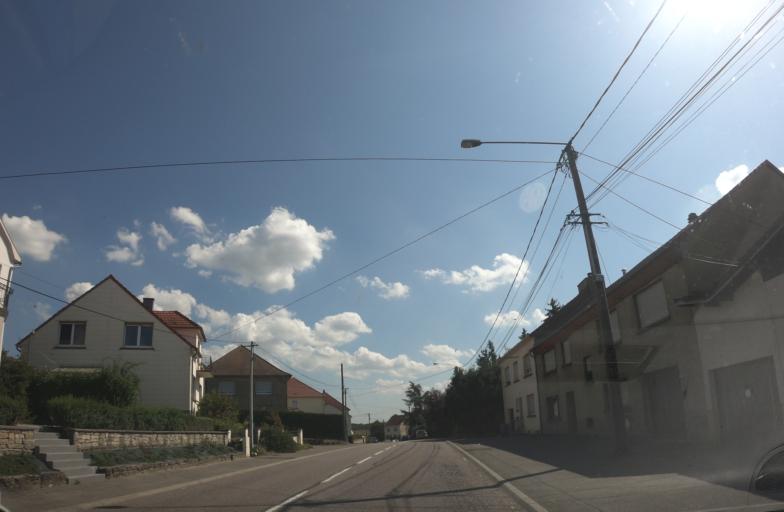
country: FR
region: Lorraine
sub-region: Departement de la Moselle
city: Hundling
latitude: 49.1071
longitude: 6.9846
